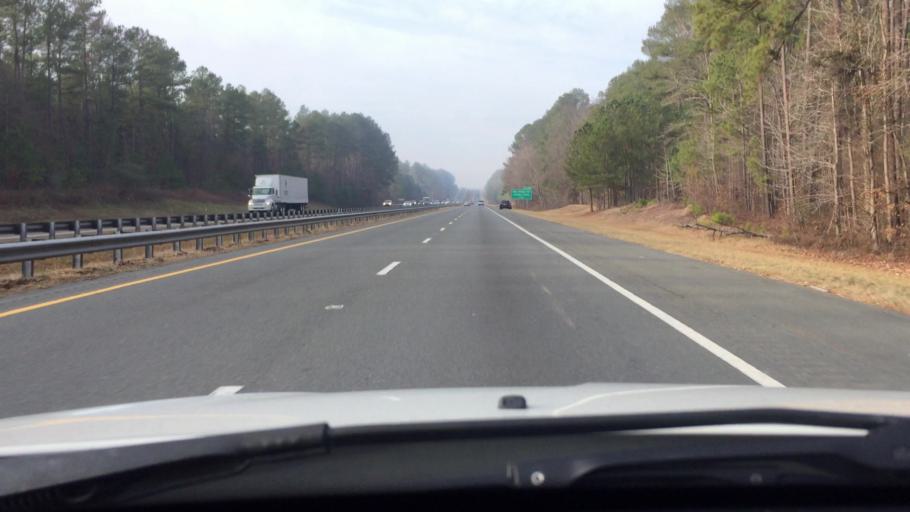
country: US
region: North Carolina
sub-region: Chatham County
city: Pittsboro
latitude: 35.6406
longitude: -79.0317
